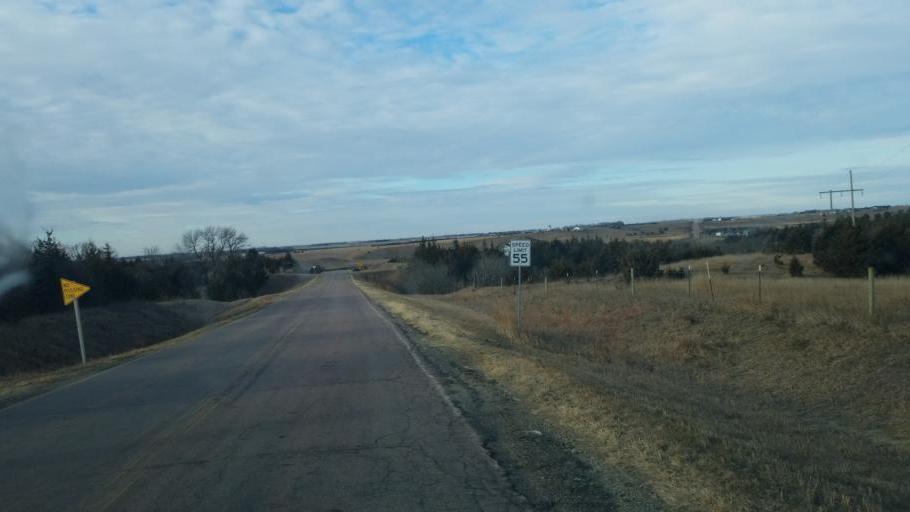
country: US
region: South Dakota
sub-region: Yankton County
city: Yankton
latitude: 42.9811
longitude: -97.3980
